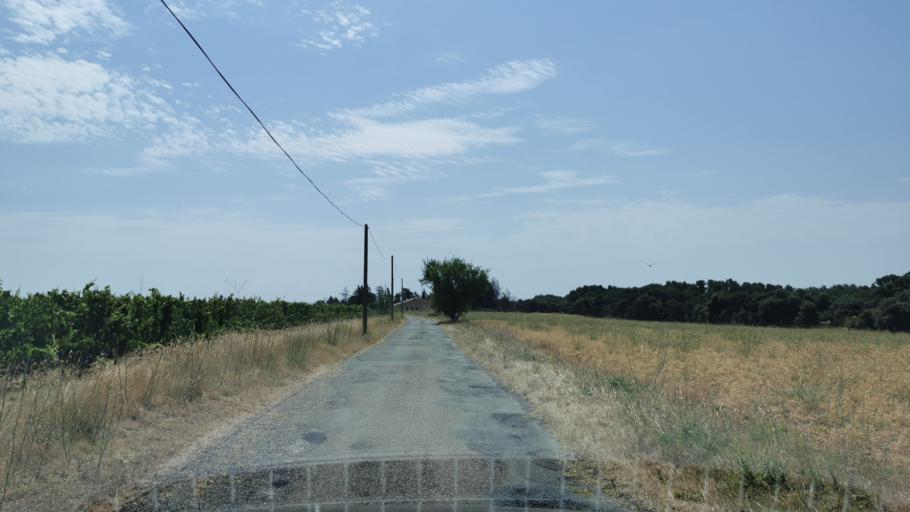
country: FR
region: Languedoc-Roussillon
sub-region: Departement de l'Aude
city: Bize-Minervois
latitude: 43.2970
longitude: 2.8780
